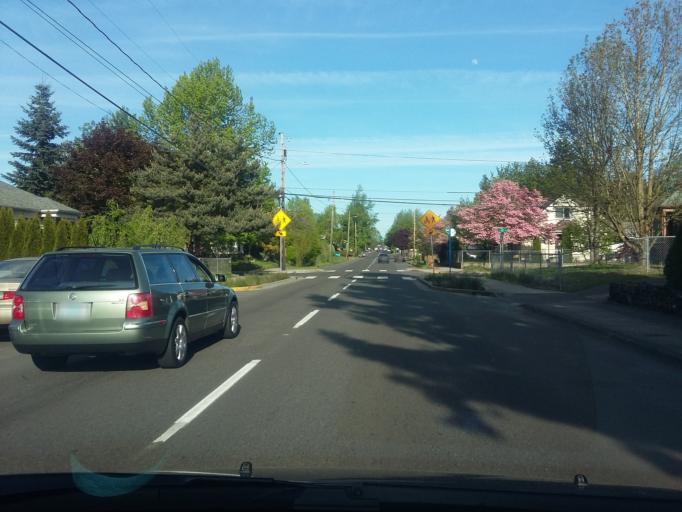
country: US
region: Oregon
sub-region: Multnomah County
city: Lents
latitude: 45.5183
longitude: -122.5758
